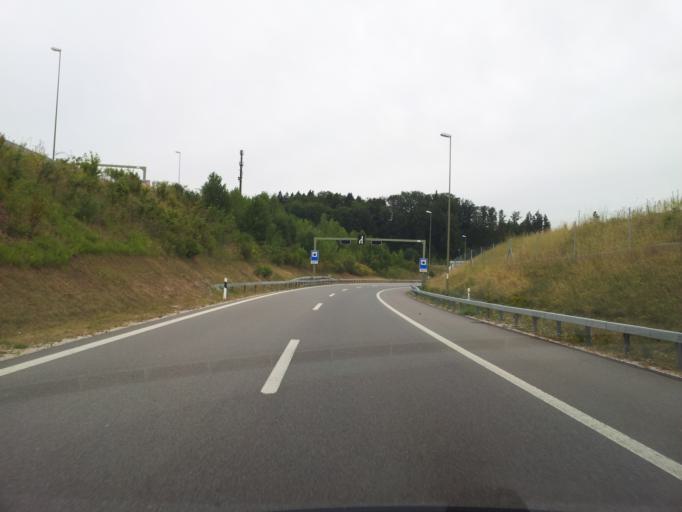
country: CH
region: Zurich
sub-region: Bezirk Affoltern
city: Wettswil / Wettswil (Dorf)
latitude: 47.3402
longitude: 8.4593
